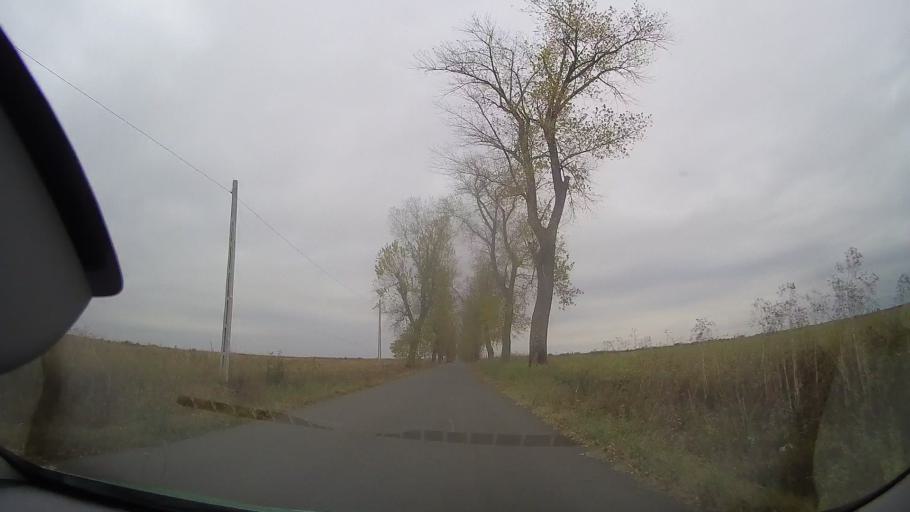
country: RO
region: Braila
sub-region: Comuna Ciocile
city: Ciocile
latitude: 44.8110
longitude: 27.2832
